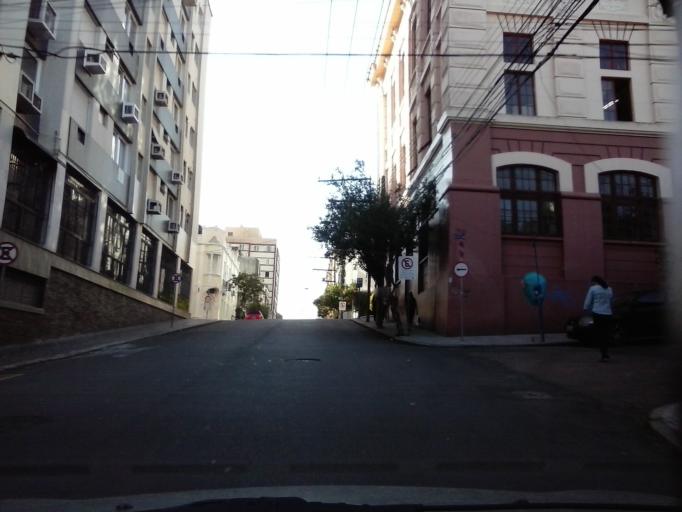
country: BR
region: Rio Grande do Sul
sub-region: Porto Alegre
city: Porto Alegre
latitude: -30.0352
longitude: -51.2378
